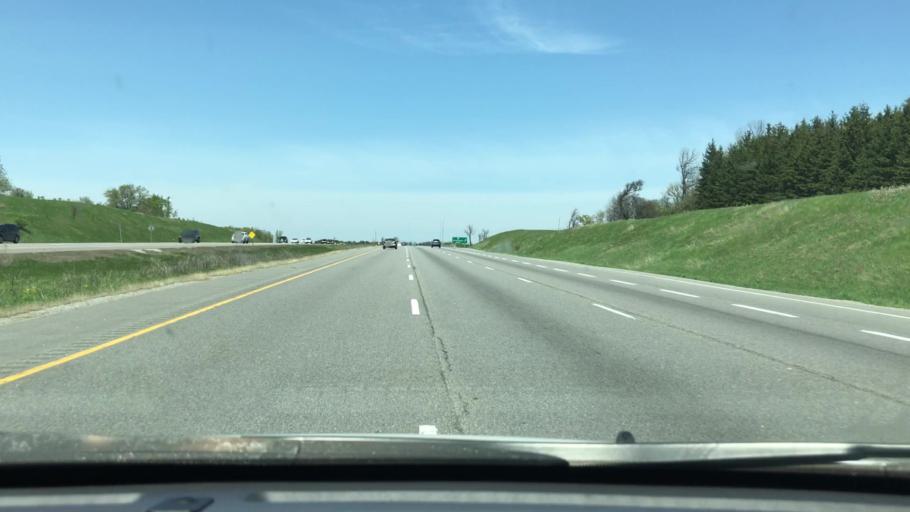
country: CA
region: Ontario
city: Newmarket
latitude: 43.9705
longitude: -79.3924
